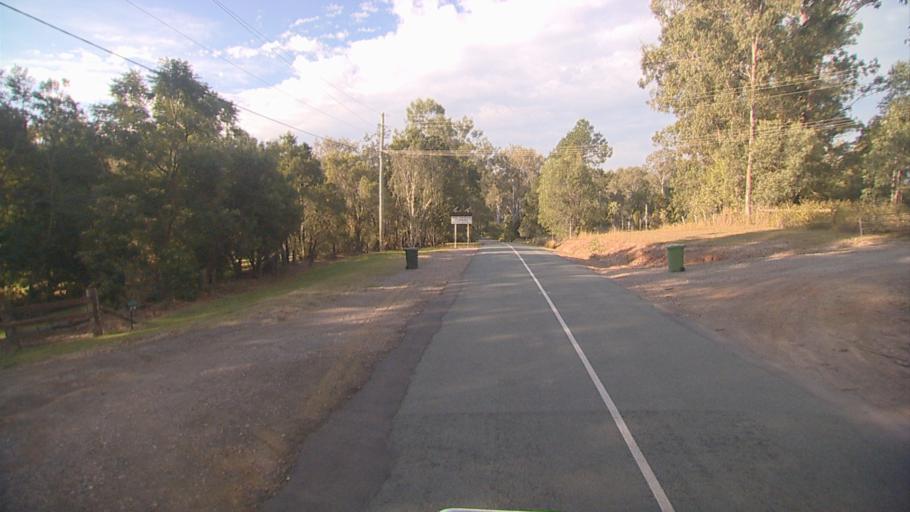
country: AU
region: Queensland
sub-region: Gold Coast
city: Ormeau Hills
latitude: -27.8446
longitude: 153.1540
